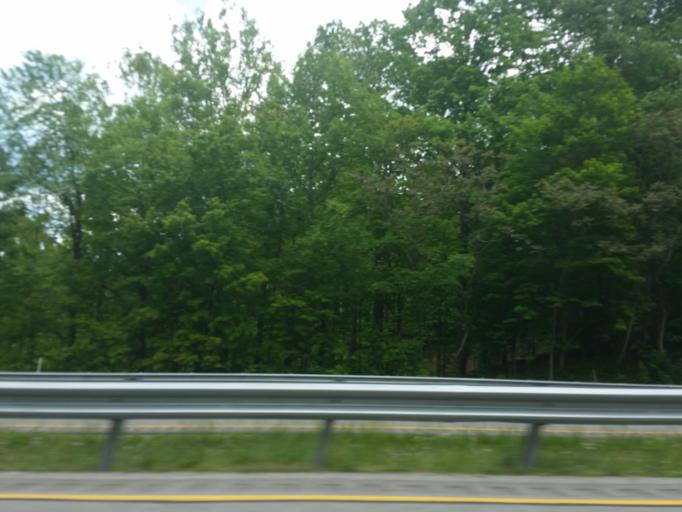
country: US
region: West Virginia
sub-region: Kanawha County
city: Charleston
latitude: 38.4004
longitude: -81.6173
